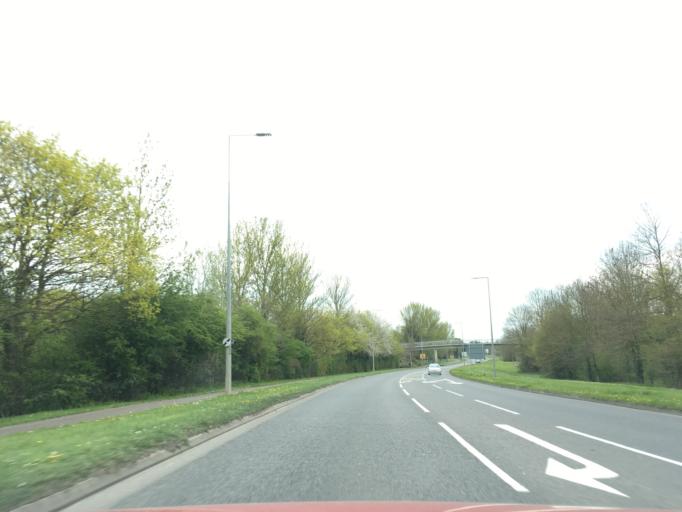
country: GB
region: England
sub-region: Milton Keynes
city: Newport Pagnell
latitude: 52.0597
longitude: -0.7297
